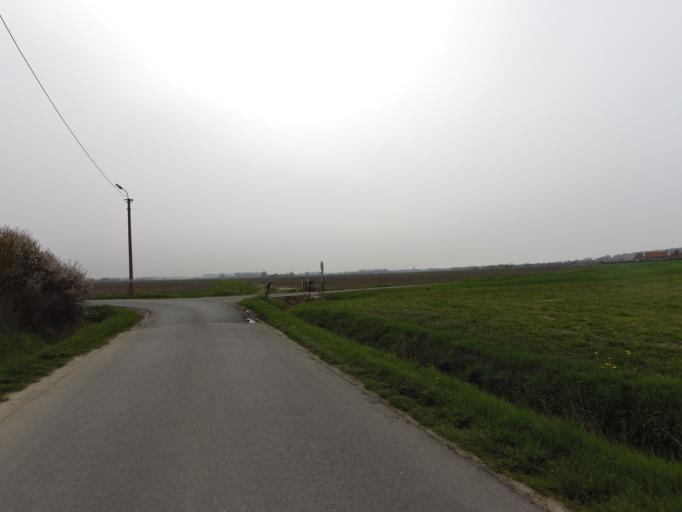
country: BE
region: Flanders
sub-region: Provincie West-Vlaanderen
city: Middelkerke
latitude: 51.1682
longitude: 2.7985
